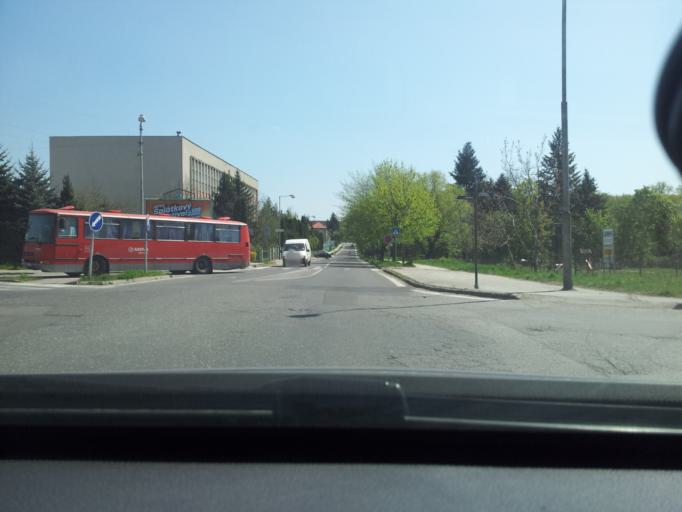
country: SK
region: Nitriansky
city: Zlate Moravce
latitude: 48.3830
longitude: 18.3891
